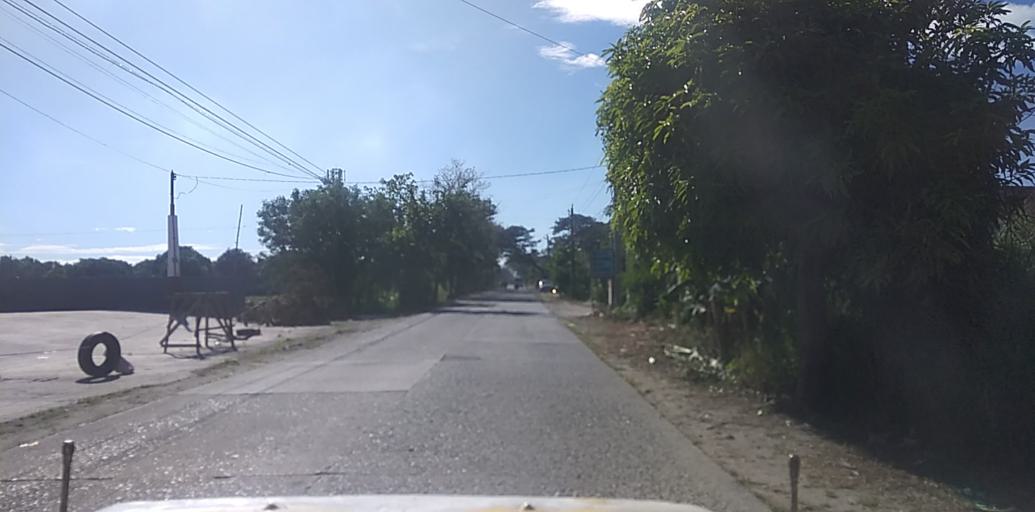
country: PH
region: Central Luzon
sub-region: Province of Pampanga
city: Mexico
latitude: 15.0777
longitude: 120.7181
